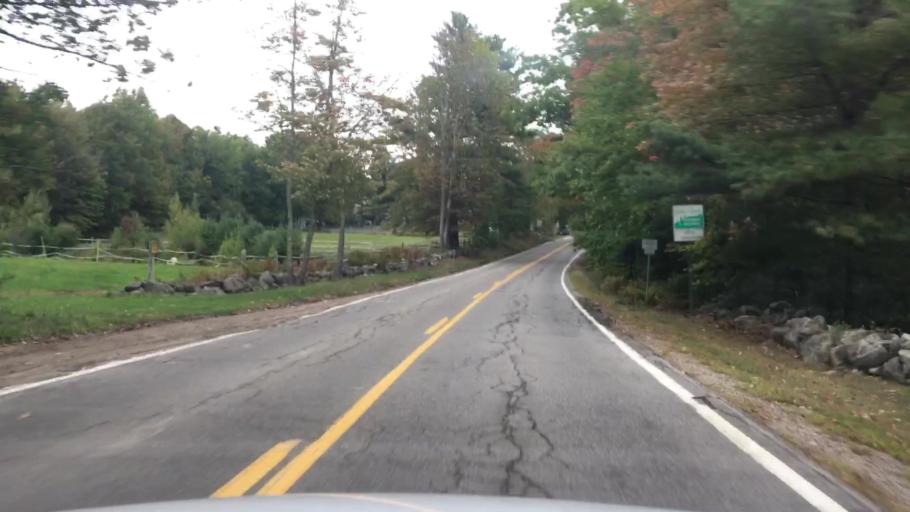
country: US
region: New Hampshire
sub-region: Carroll County
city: Effingham
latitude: 43.7592
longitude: -70.9985
